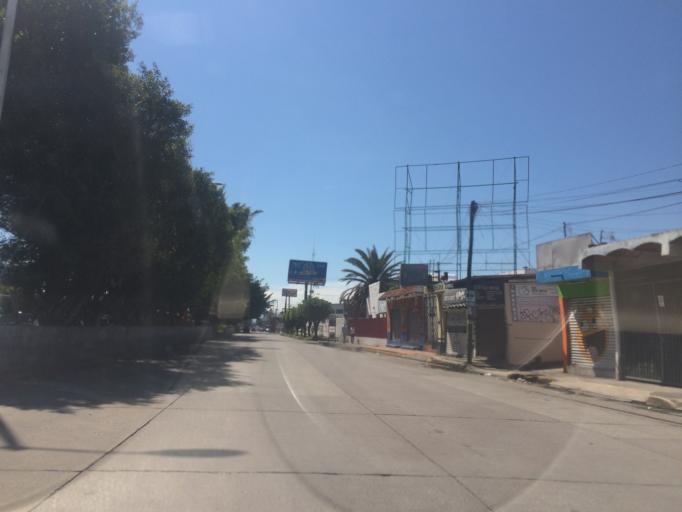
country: MX
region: Nayarit
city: Tepic
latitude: 21.5011
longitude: -104.8889
